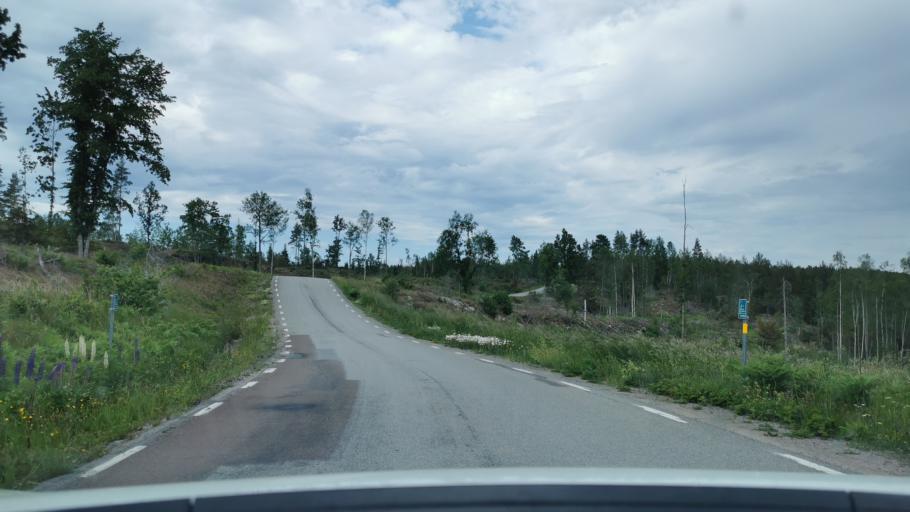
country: SE
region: Vaestra Goetaland
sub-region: Bengtsfors Kommun
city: Dals Langed
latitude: 58.8745
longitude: 12.4051
